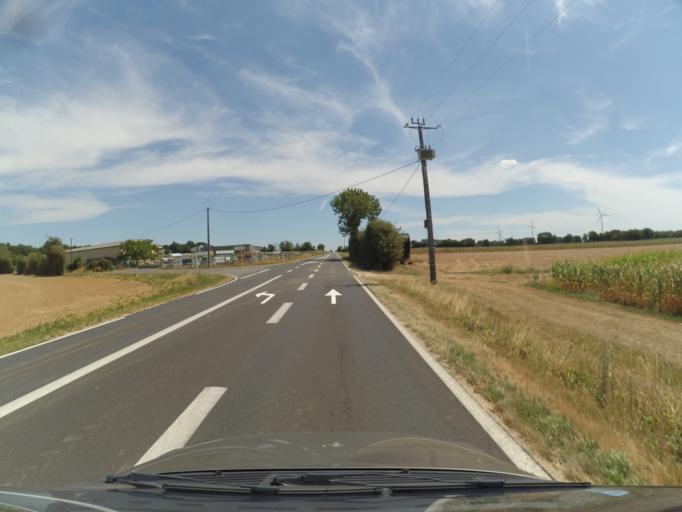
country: FR
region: Poitou-Charentes
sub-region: Departement de la Vienne
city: Saint-Maurice-la-Clouere
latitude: 46.3660
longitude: 0.4247
